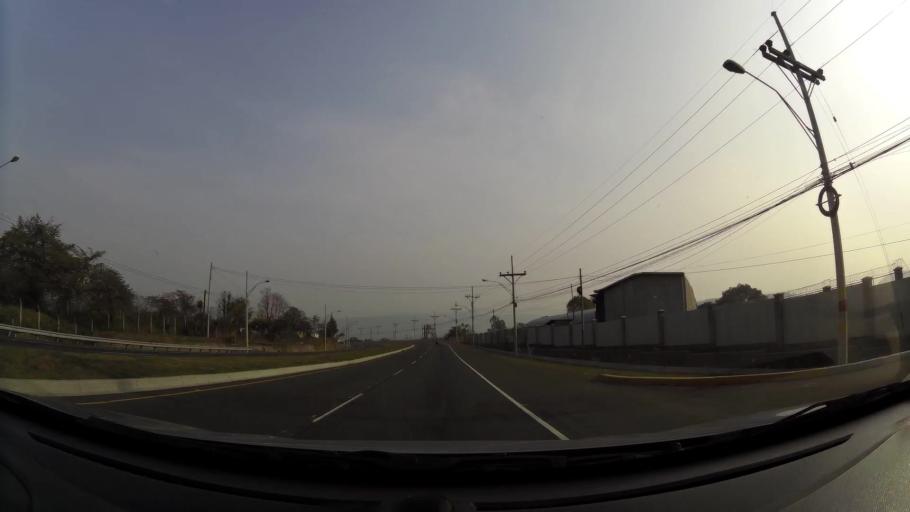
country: HN
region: Francisco Morazan
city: Tamara
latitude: 14.2118
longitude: -87.3528
